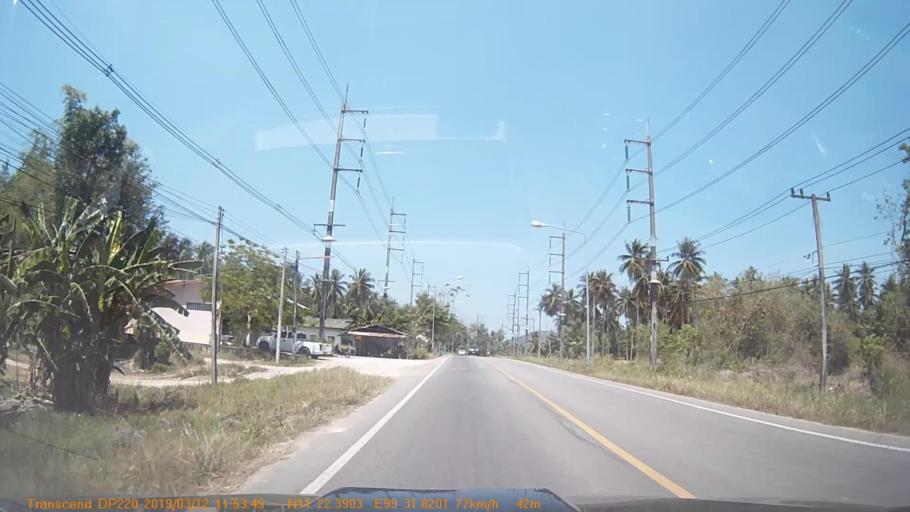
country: TH
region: Prachuap Khiri Khan
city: Thap Sakae
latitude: 11.3732
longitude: 99.5302
